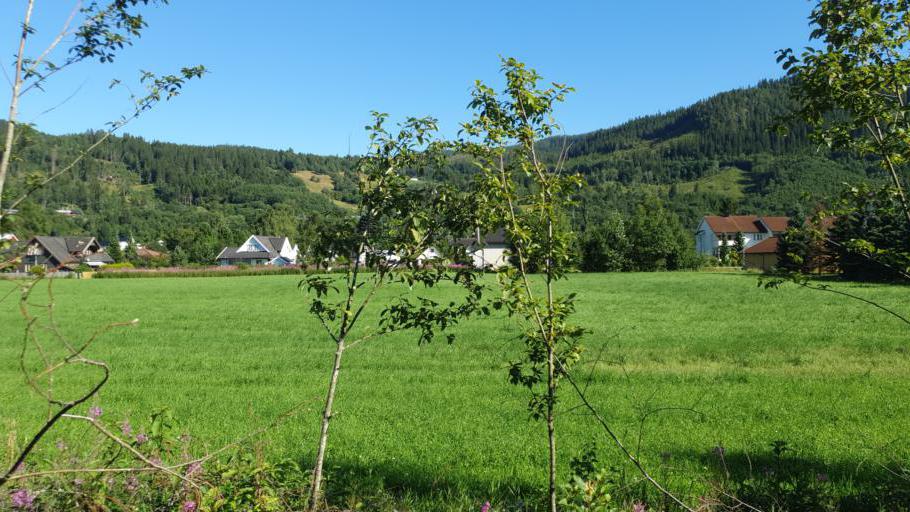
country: NO
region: Sor-Trondelag
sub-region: Orkdal
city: Orkanger
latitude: 63.2863
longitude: 9.8418
